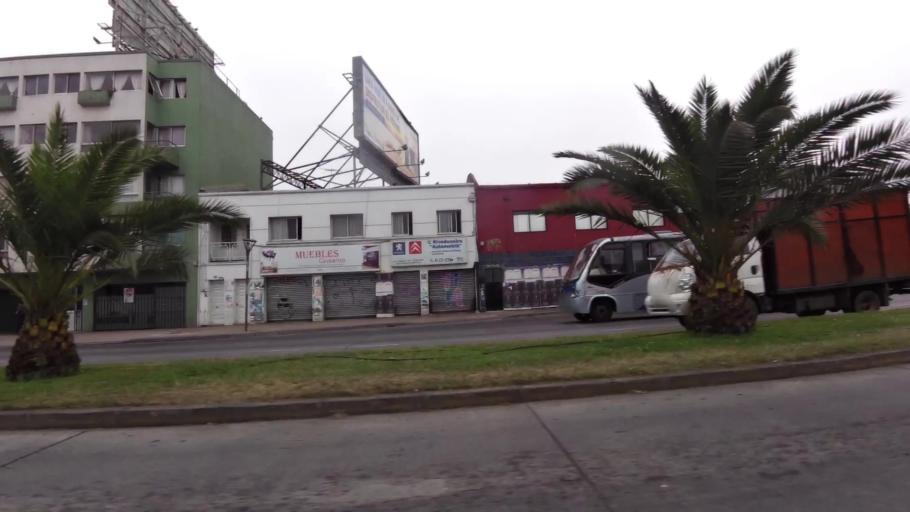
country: CL
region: Biobio
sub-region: Provincia de Concepcion
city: Concepcion
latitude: -36.8215
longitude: -73.0474
